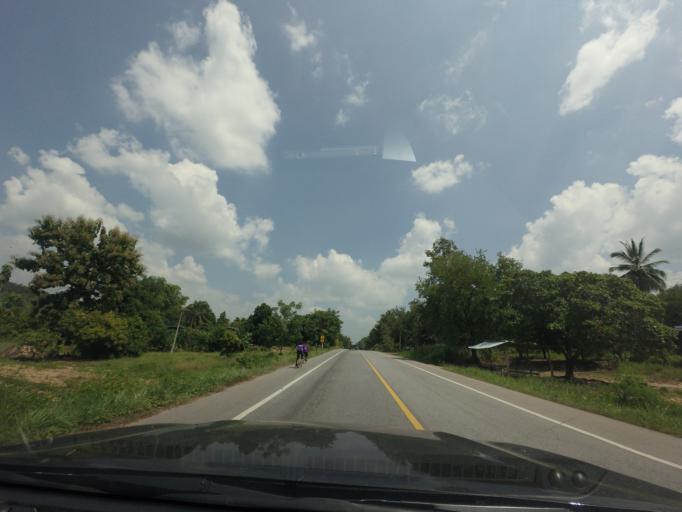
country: TH
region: Phitsanulok
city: Chat Trakan
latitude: 17.2991
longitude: 100.4193
